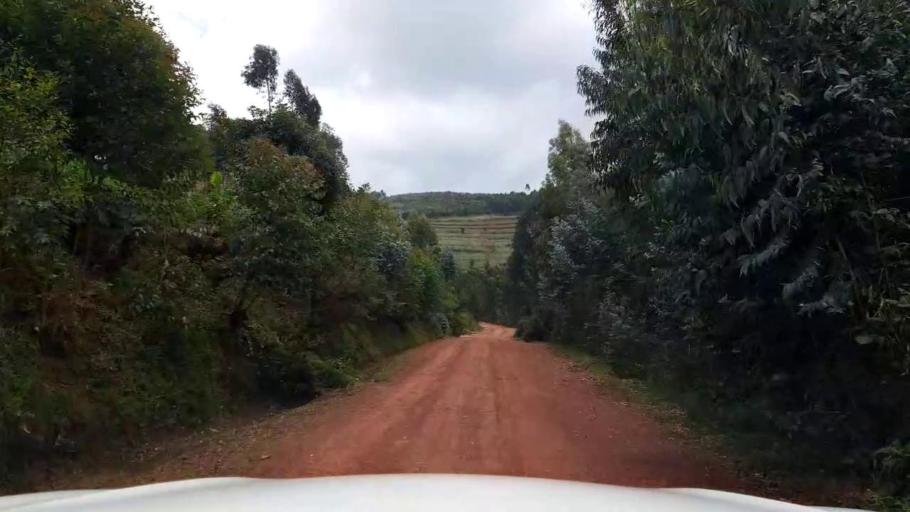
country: RW
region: Northern Province
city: Byumba
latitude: -1.4869
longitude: 29.9138
